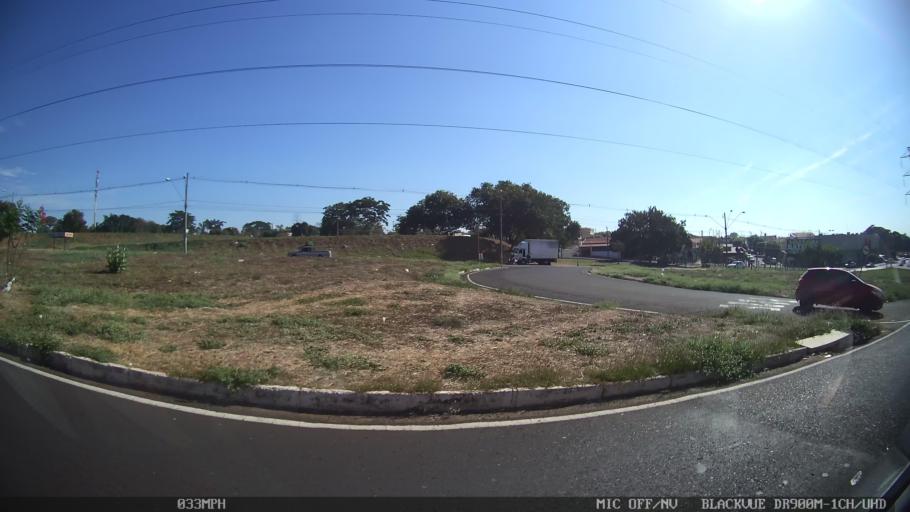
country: BR
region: Sao Paulo
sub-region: Sao Jose Do Rio Preto
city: Sao Jose do Rio Preto
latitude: -20.7677
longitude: -49.3859
